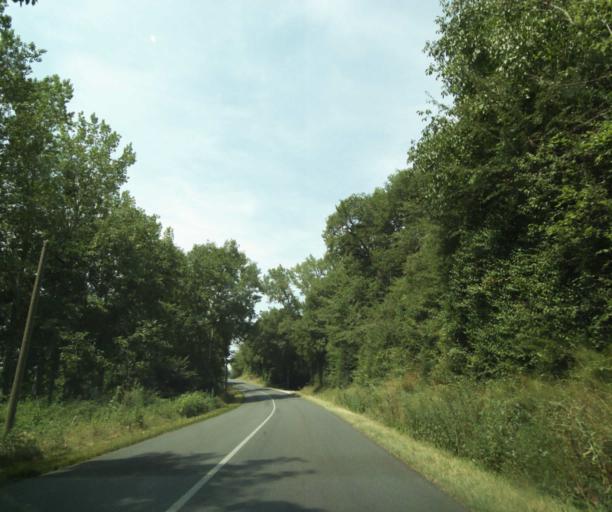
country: FR
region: Poitou-Charentes
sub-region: Departement de la Vienne
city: Lussac-les-Chateaux
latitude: 46.4308
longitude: 0.6852
